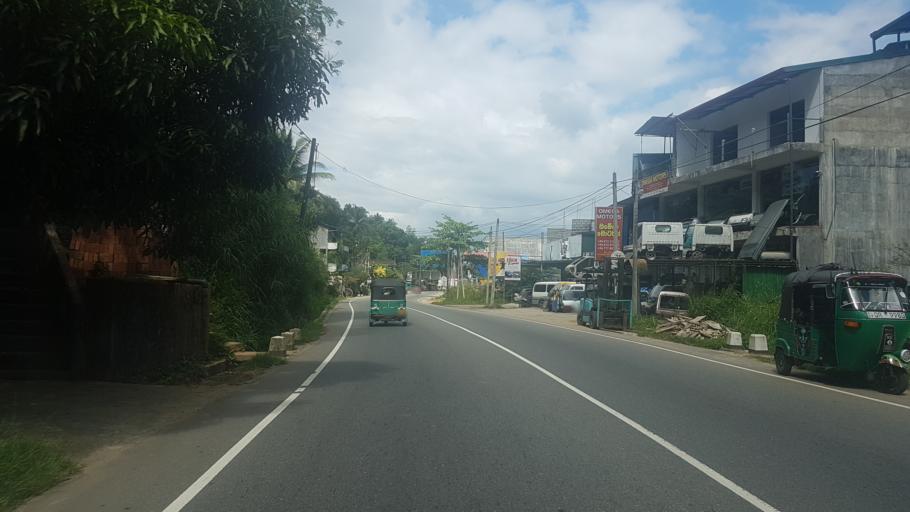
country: LK
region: Central
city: Gampola
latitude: 7.2016
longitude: 80.5993
